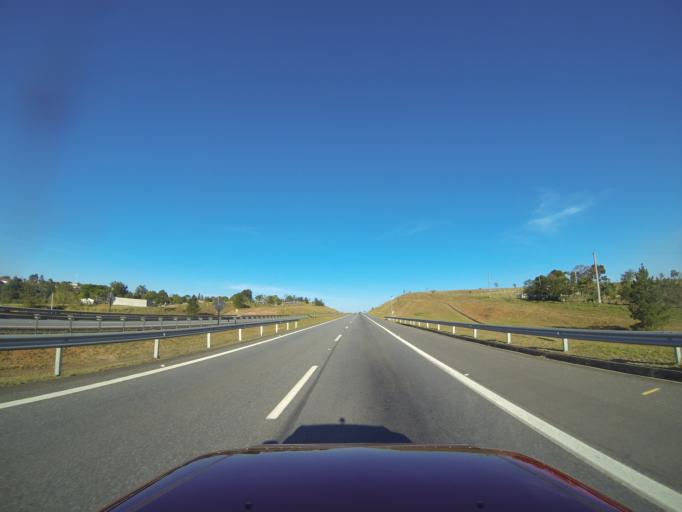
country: BR
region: Sao Paulo
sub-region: Jacarei
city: Jacarei
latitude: -23.3181
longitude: -46.0419
